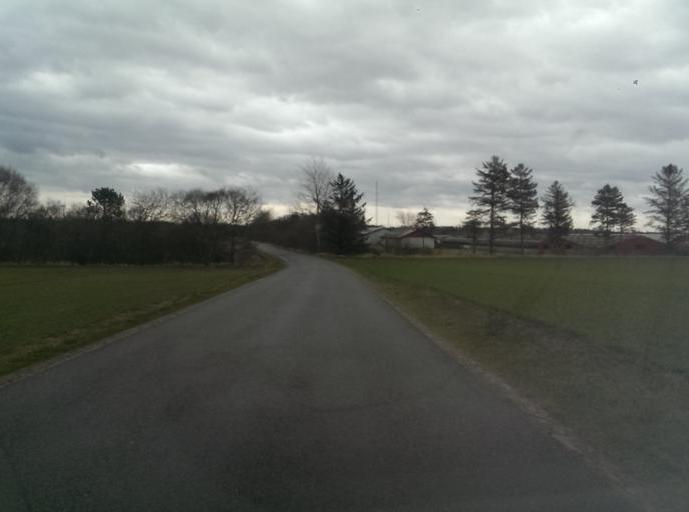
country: DK
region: Central Jutland
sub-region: Ringkobing-Skjern Kommune
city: Ringkobing
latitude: 56.1279
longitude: 8.3212
